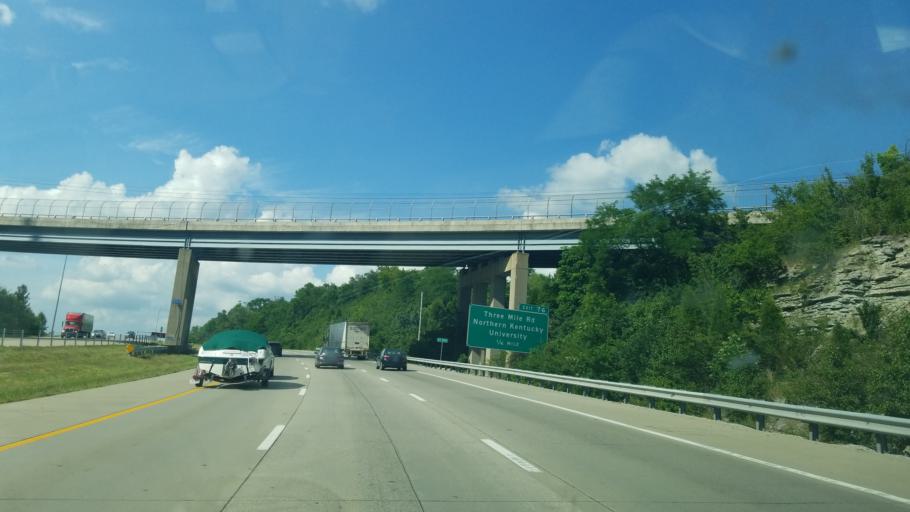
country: US
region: Kentucky
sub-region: Campbell County
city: Highland Heights
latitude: 39.0298
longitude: -84.4710
